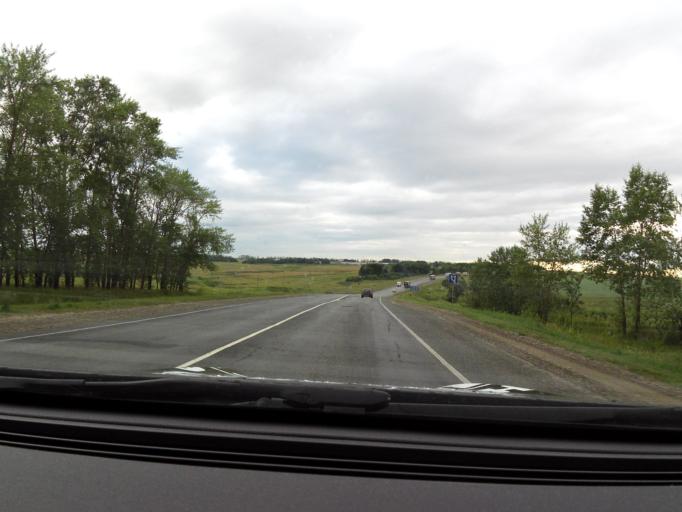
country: RU
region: Chuvashia
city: Tsivil'sk
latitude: 55.7902
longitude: 47.6824
